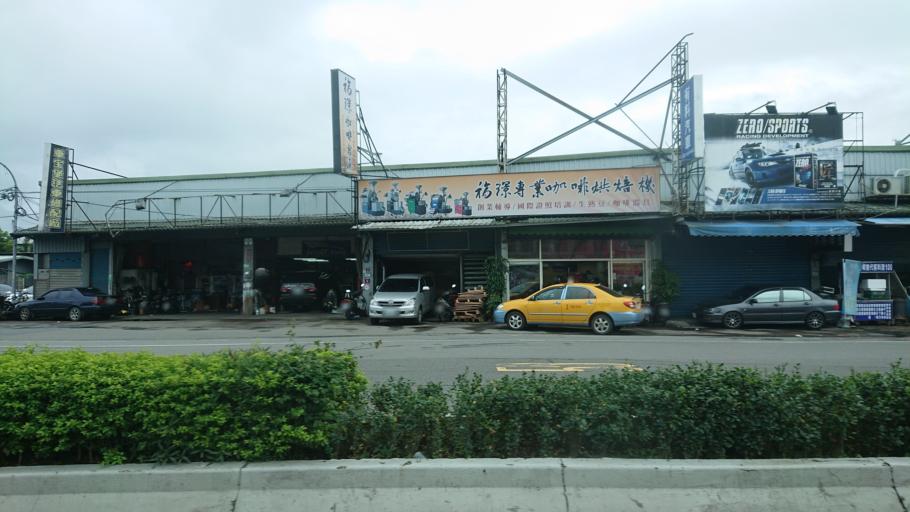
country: TW
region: Taipei
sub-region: Taipei
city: Banqiao
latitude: 24.9795
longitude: 121.4518
